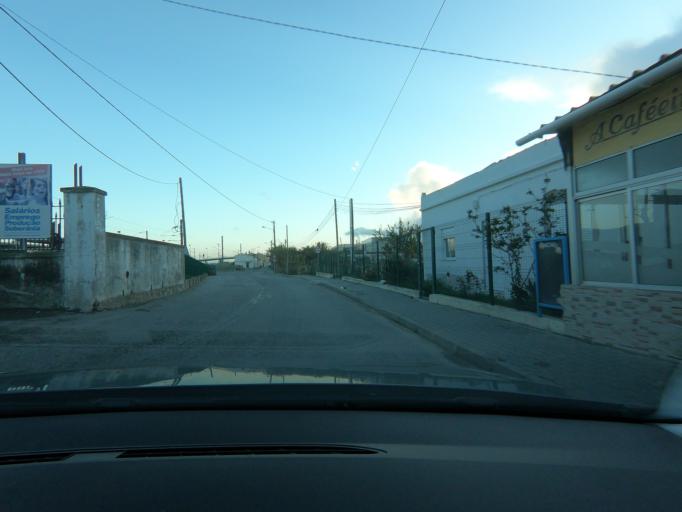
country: PT
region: Lisbon
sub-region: Vila Franca de Xira
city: Castanheira do Ribatejo
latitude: 39.0056
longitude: -8.9541
